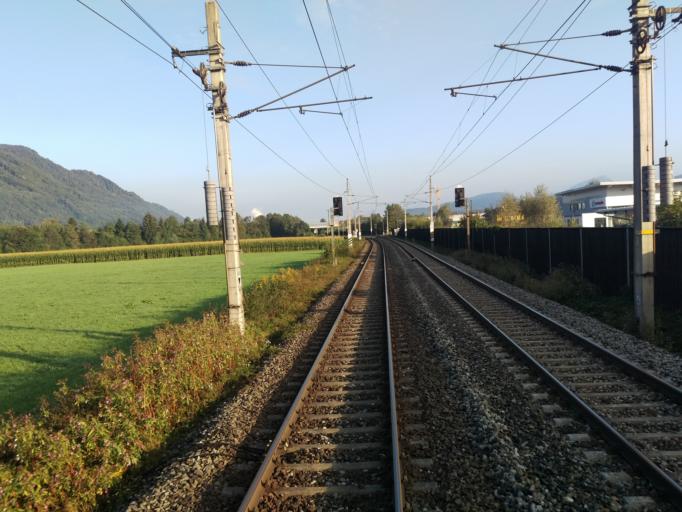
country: AT
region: Salzburg
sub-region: Politischer Bezirk Hallein
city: Kuchl
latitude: 47.6351
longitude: 13.1380
